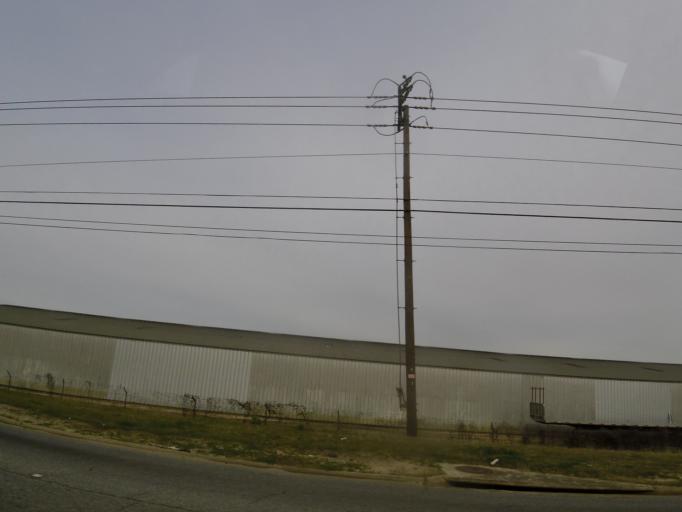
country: US
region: Georgia
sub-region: Decatur County
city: Bainbridge
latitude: 30.9133
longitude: -84.5853
